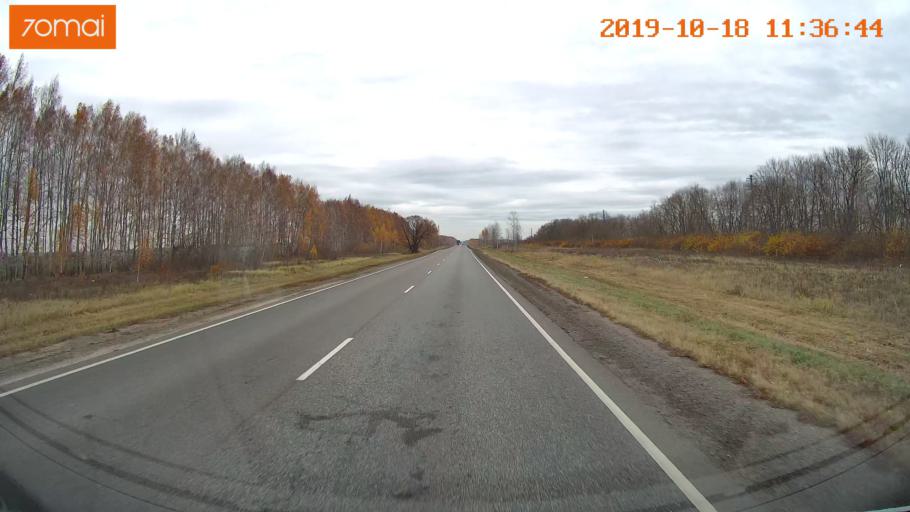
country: RU
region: Rjazan
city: Oktyabr'skiy
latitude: 54.1441
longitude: 38.8139
